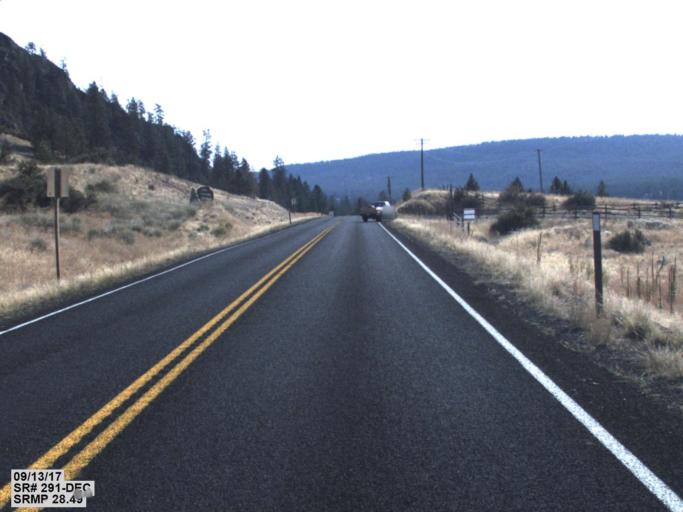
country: US
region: Washington
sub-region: Spokane County
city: Fairchild Air Force Base
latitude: 47.8386
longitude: -117.7630
